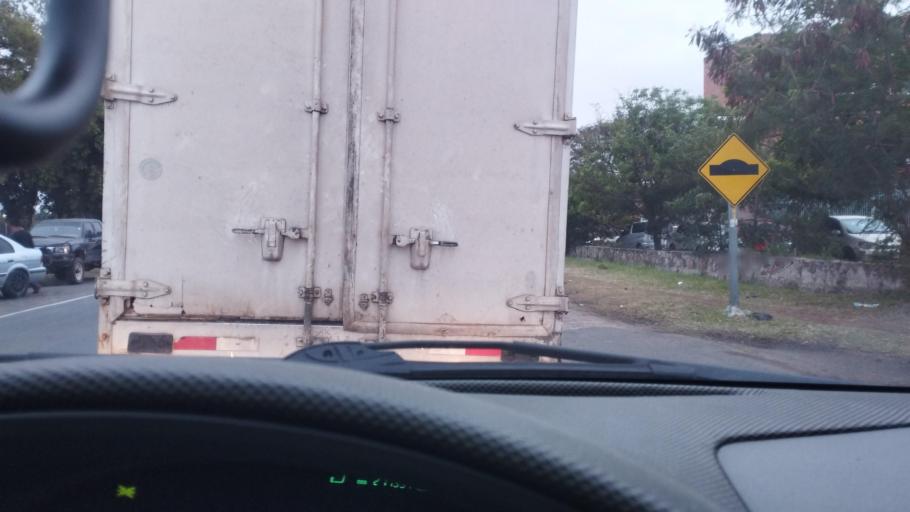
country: PY
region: Central
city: Fernando de la Mora
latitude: -25.2703
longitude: -57.5216
